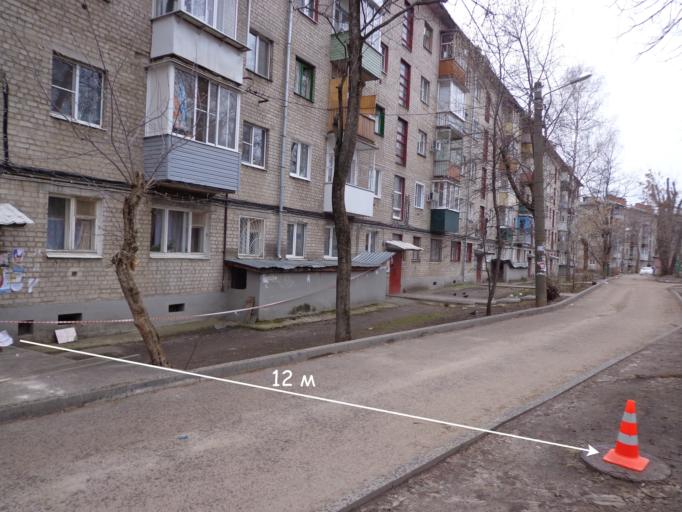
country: RU
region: Voronezj
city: Voronezh
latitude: 51.6992
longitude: 39.2268
